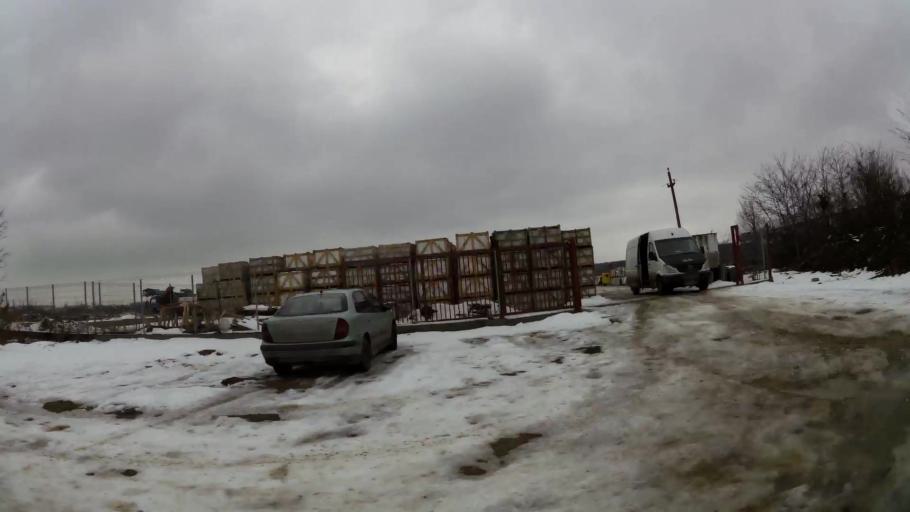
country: RO
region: Ilfov
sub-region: Comuna Mogosoaia
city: Mogosoaia
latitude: 44.5080
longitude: 26.0085
